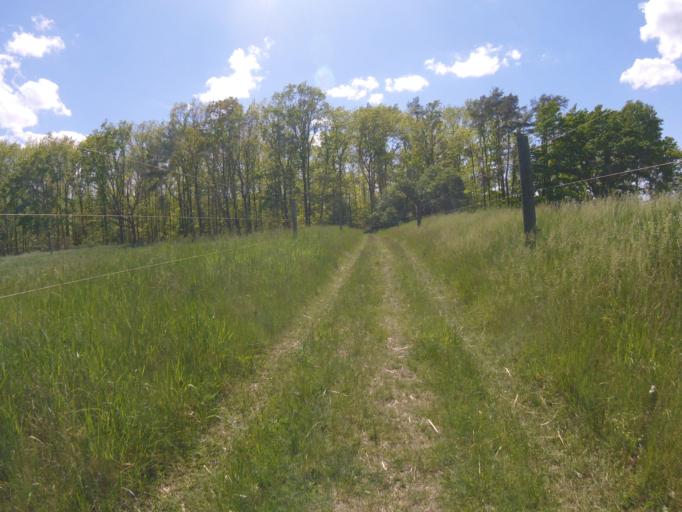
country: DE
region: Brandenburg
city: Teupitz
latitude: 52.1254
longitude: 13.6179
